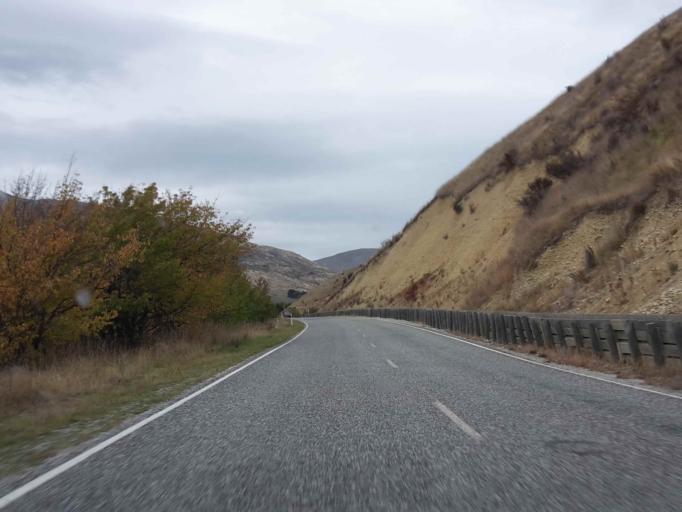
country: NZ
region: Otago
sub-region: Queenstown-Lakes District
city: Wanaka
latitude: -44.8212
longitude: 169.0629
